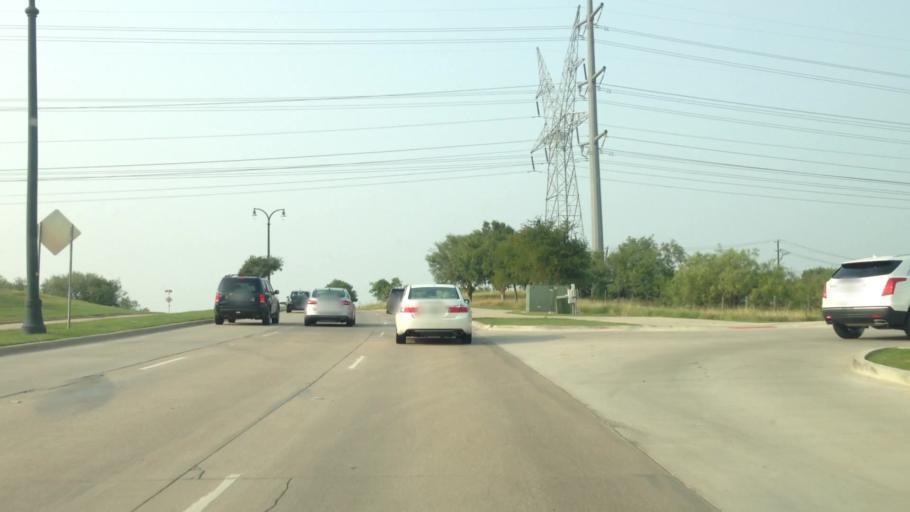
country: US
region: Texas
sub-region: Denton County
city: The Colony
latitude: 33.0591
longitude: -96.8628
